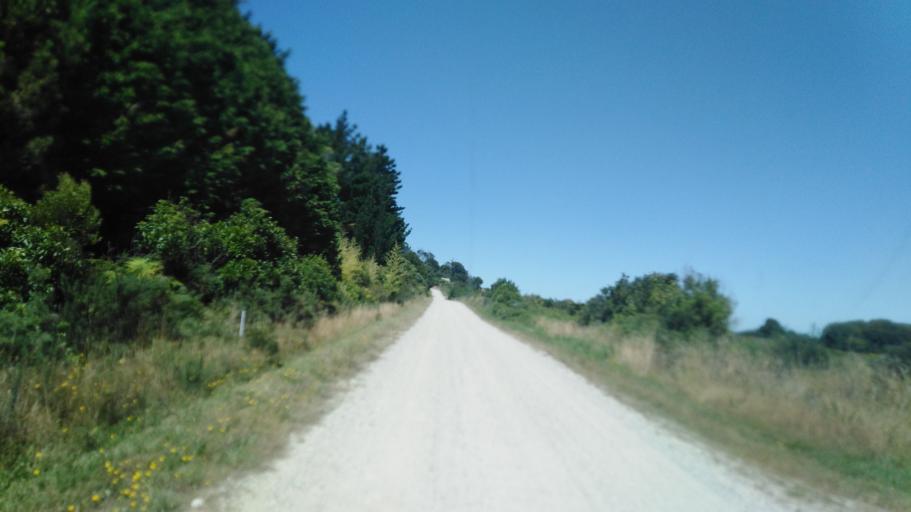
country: NZ
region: West Coast
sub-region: Buller District
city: Westport
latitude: -41.2632
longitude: 172.1142
